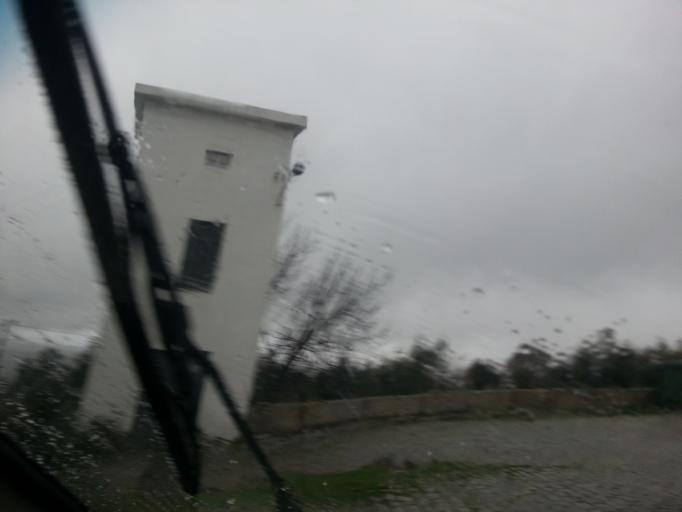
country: PT
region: Guarda
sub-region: Fornos de Algodres
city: Fornos de Algodres
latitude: 40.5387
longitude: -7.4620
